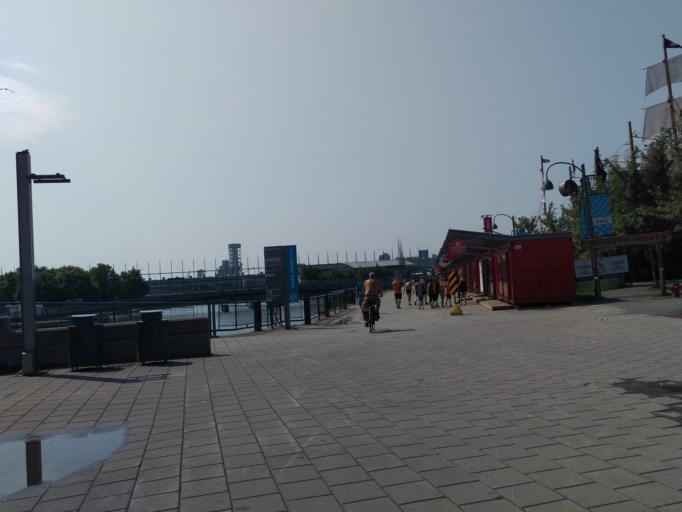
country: CA
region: Quebec
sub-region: Montreal
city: Montreal
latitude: 45.5094
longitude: -73.5498
